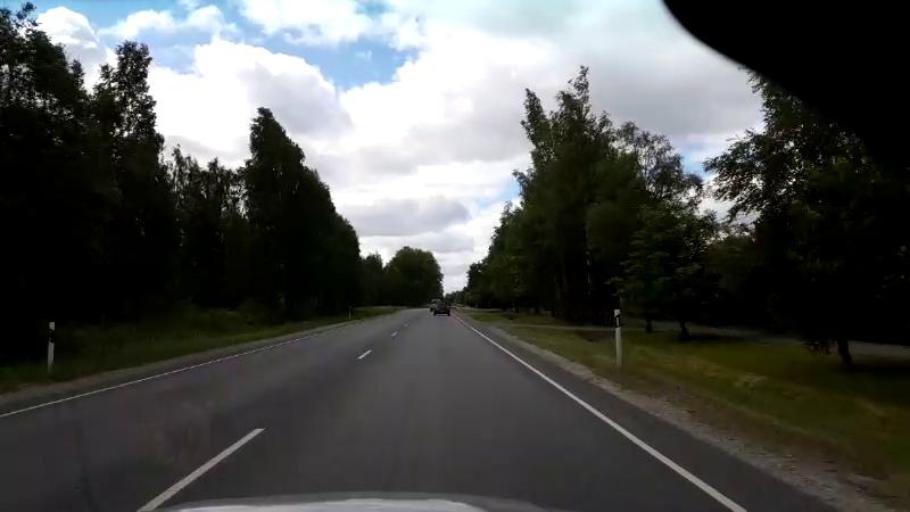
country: EE
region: Paernumaa
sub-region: Sauga vald
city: Sauga
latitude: 58.4194
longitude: 24.4945
